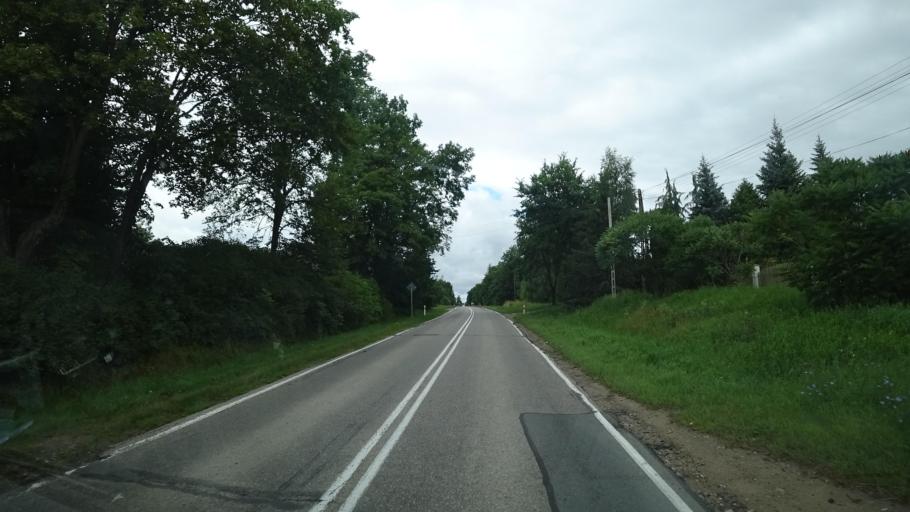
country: PL
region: Warmian-Masurian Voivodeship
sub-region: Powiat olecki
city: Olecko
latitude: 54.0702
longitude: 22.4792
